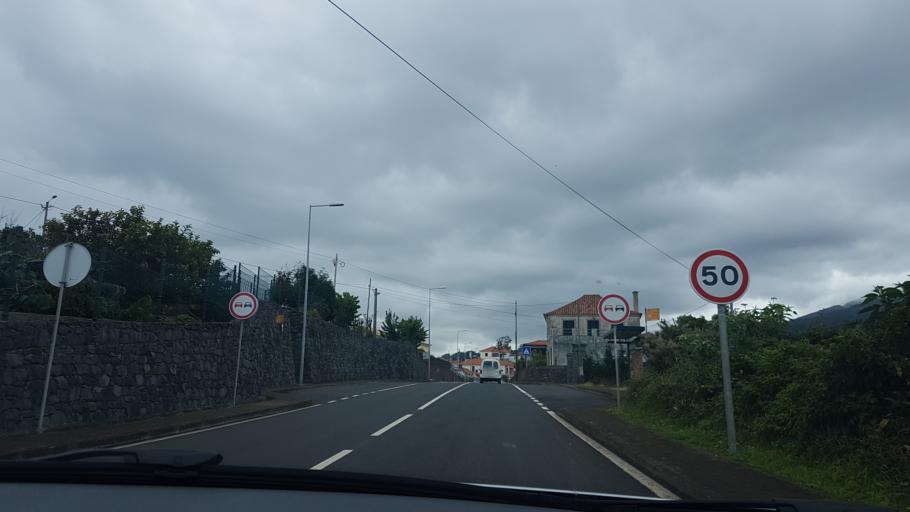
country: PT
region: Madeira
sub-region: Santana
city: Santana
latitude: 32.8186
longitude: -16.8875
